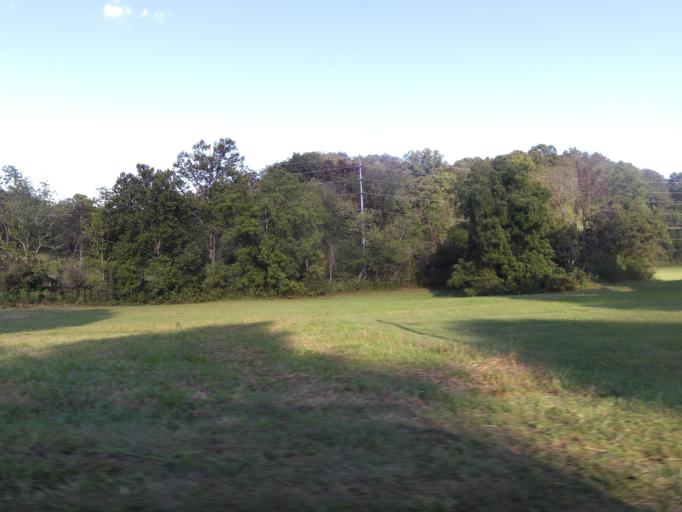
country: US
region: Tennessee
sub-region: Union County
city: Condon
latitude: 36.1982
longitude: -83.8300
